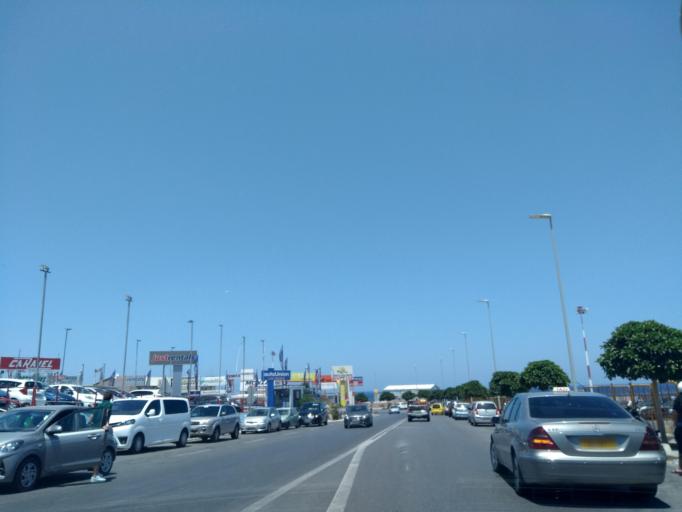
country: GR
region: Crete
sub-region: Nomos Irakleiou
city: Nea Alikarnassos
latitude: 35.3367
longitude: 25.1722
